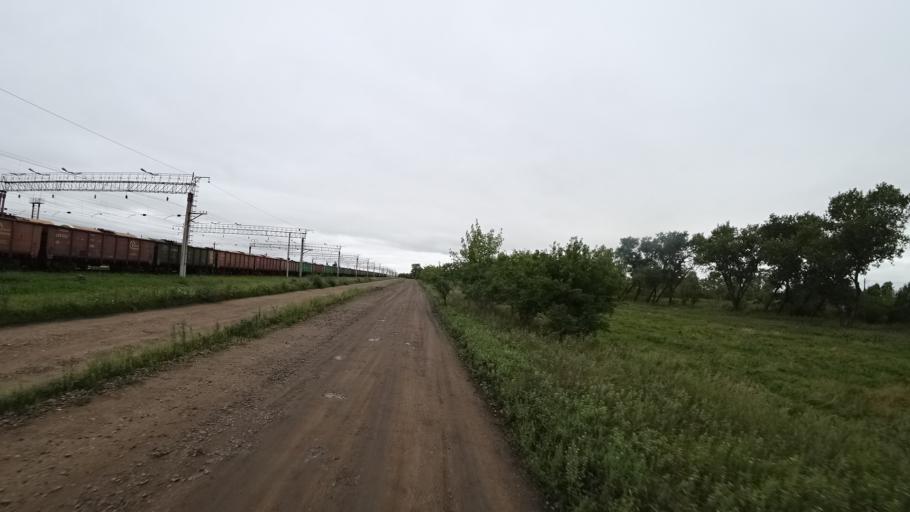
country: RU
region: Primorskiy
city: Chernigovka
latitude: 44.3404
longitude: 132.5333
